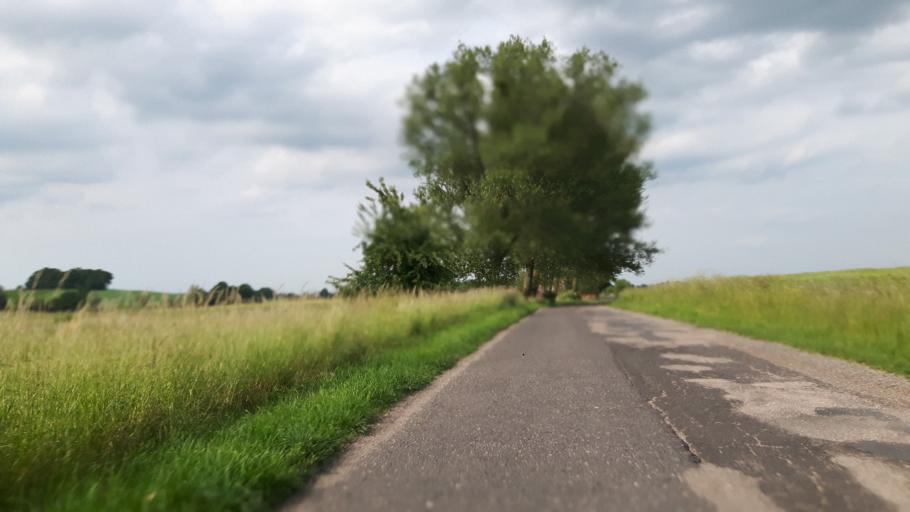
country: PL
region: West Pomeranian Voivodeship
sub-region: Powiat gryficki
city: Gryfice
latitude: 53.8213
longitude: 15.1352
